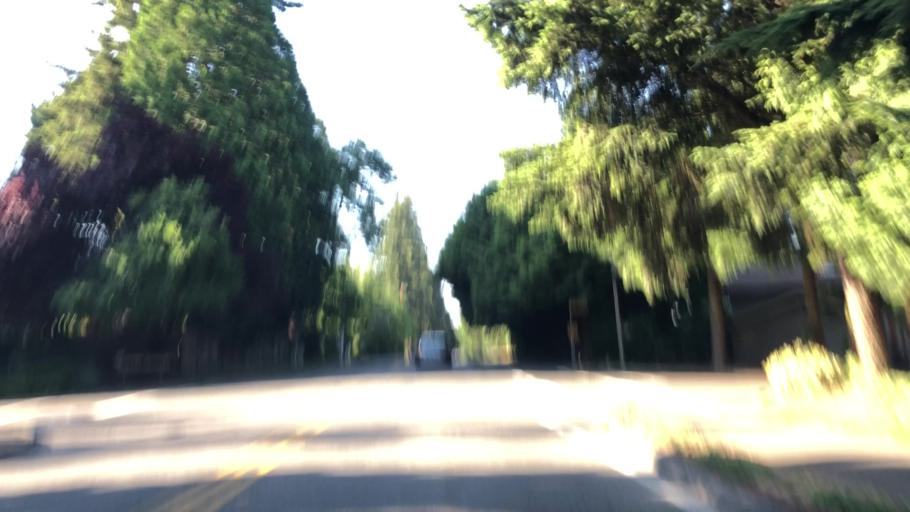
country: US
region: Washington
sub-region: King County
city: Woodinville
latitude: 47.7610
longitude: -122.1636
